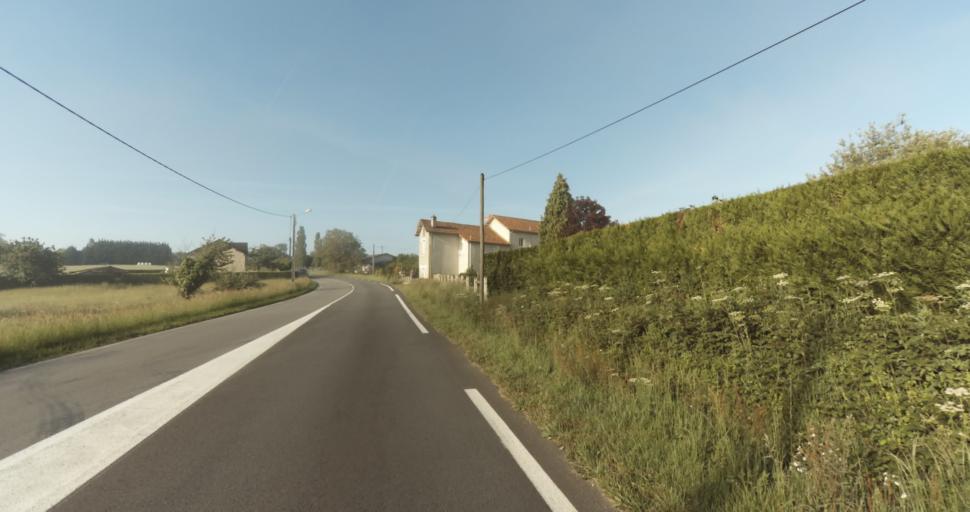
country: FR
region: Limousin
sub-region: Departement de la Haute-Vienne
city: Condat-sur-Vienne
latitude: 45.7851
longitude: 1.2888
